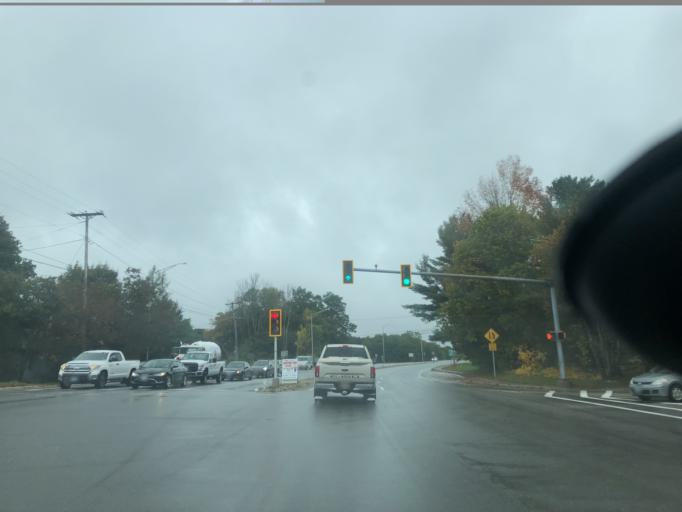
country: US
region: New Hampshire
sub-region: Strafford County
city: Dover
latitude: 43.1834
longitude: -70.8904
